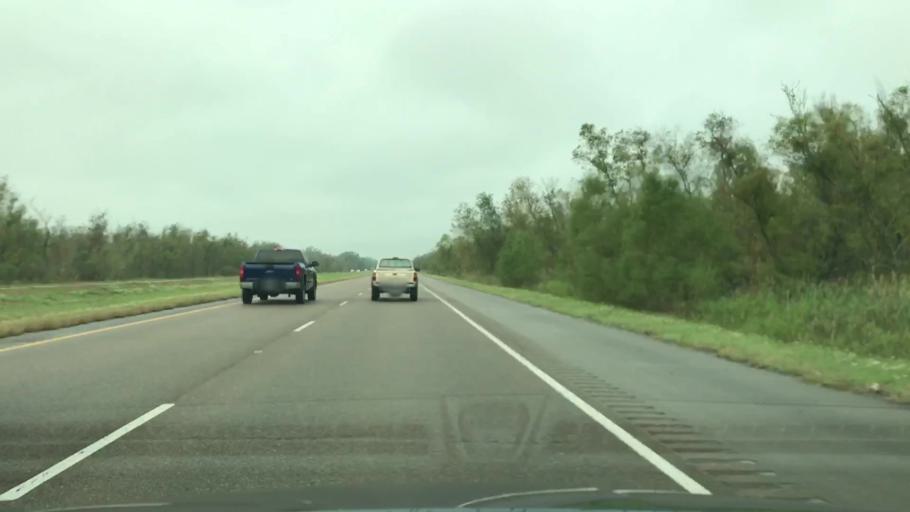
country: US
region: Louisiana
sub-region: Terrebonne Parish
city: Bayou Cane
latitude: 29.6867
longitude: -90.7081
